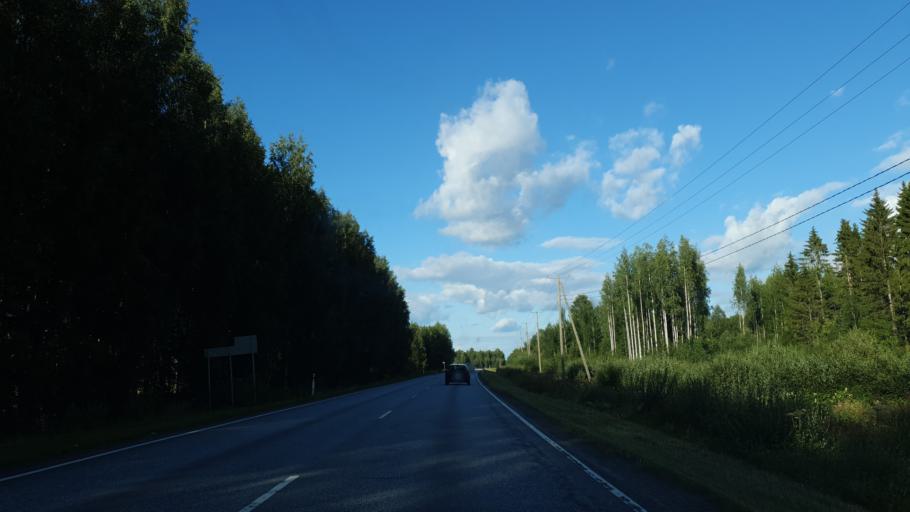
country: FI
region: North Karelia
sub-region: Joensuu
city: Outokumpu
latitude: 62.5703
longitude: 29.1582
